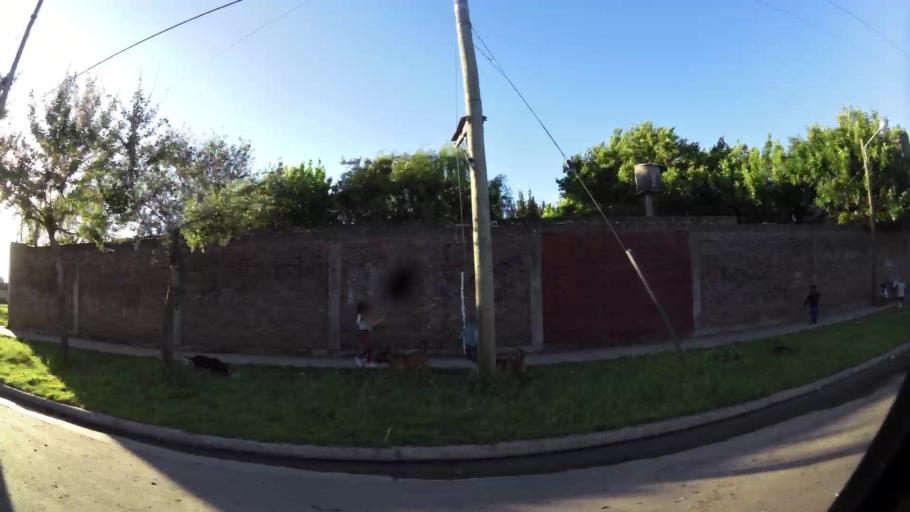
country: AR
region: Buenos Aires
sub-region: Partido de Almirante Brown
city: Adrogue
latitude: -34.7703
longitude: -58.3308
